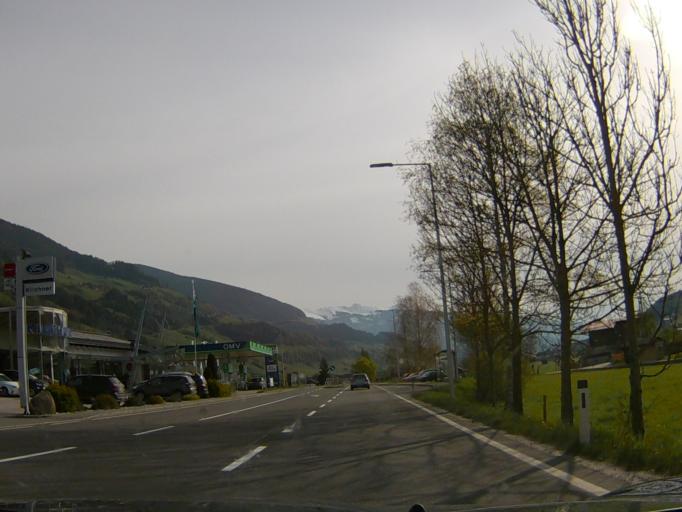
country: AT
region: Salzburg
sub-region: Politischer Bezirk Zell am See
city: Bramberg am Wildkogel
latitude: 47.2637
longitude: 12.3303
